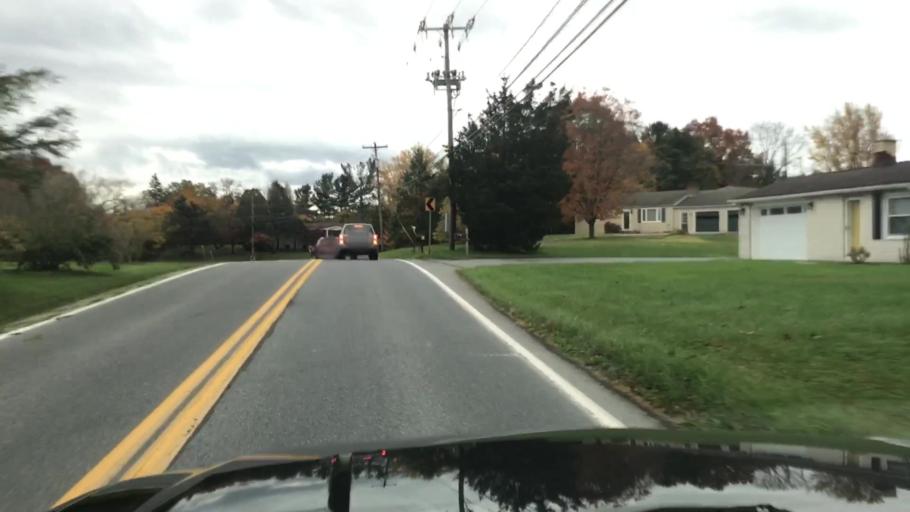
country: US
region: Pennsylvania
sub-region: Cumberland County
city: Shiremanstown
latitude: 40.1728
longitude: -76.9425
